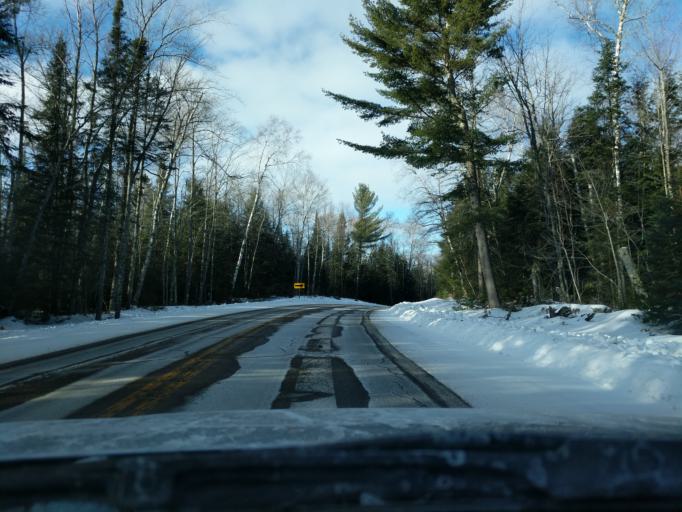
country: US
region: Wisconsin
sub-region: Vilas County
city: Eagle River
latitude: 45.7651
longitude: -89.0677
